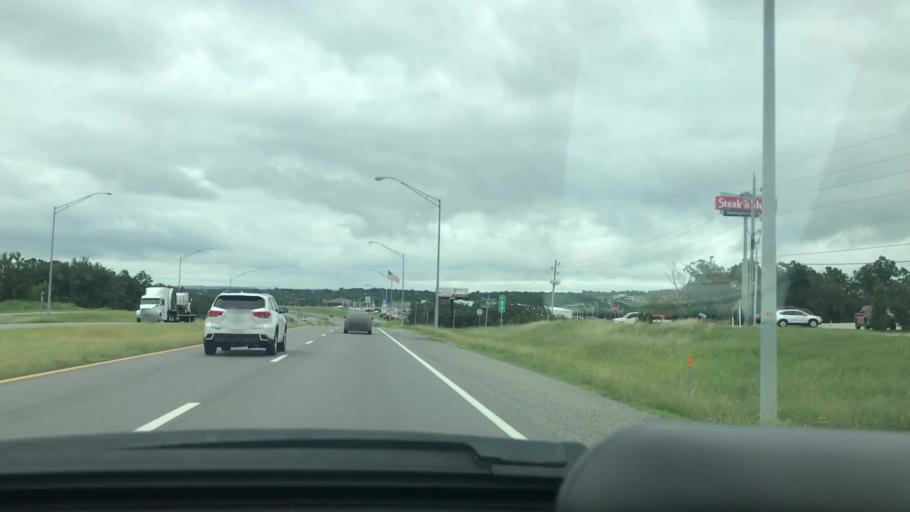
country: US
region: Oklahoma
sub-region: Pittsburg County
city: McAlester
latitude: 34.8980
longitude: -95.7593
